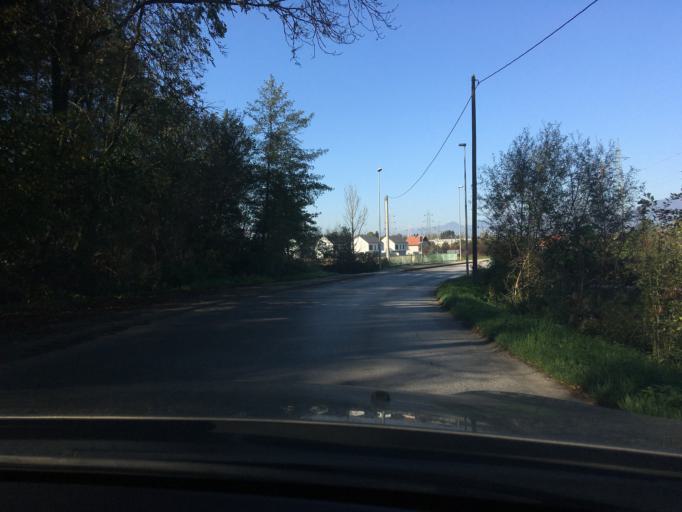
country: SI
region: Domzale
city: Vir
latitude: 46.1416
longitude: 14.6100
